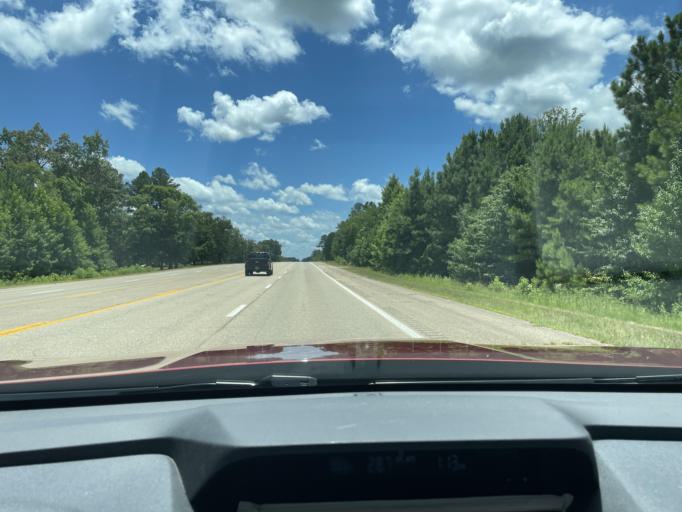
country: US
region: Arkansas
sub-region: Drew County
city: Monticello
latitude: 33.6822
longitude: -91.8054
